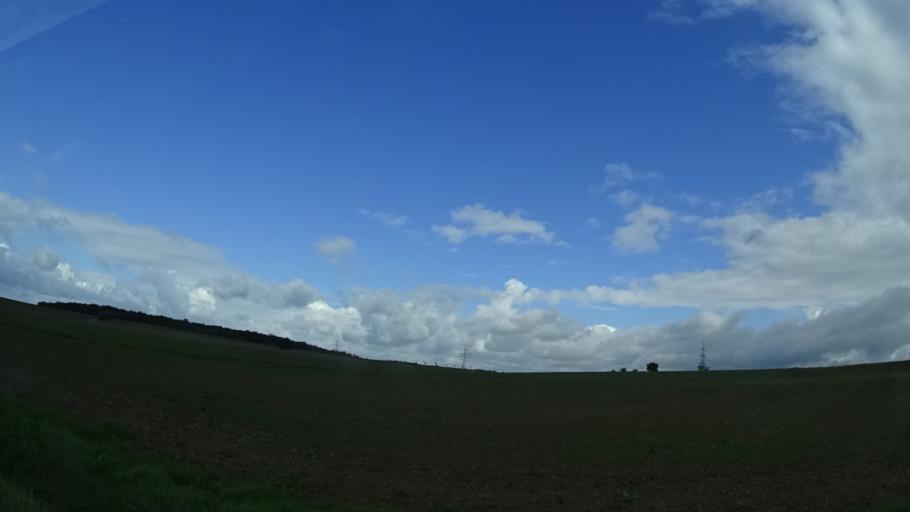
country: DE
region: Bavaria
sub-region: Regierungsbezirk Unterfranken
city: Frankenwinheim
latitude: 49.8616
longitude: 10.3000
